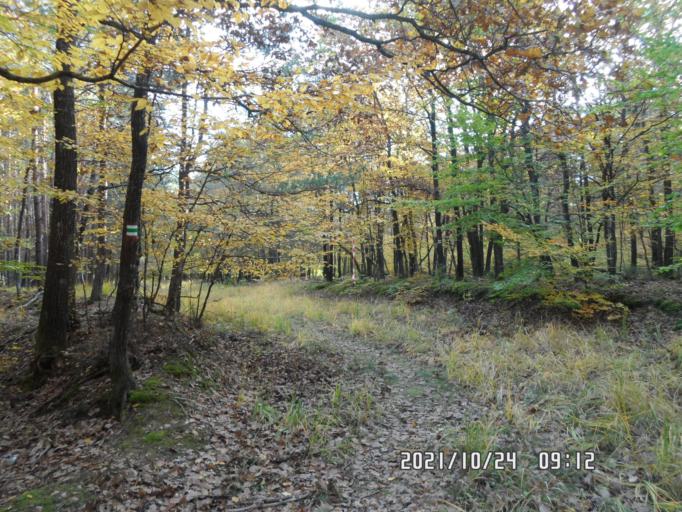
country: SI
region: Hodos-Hodos
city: Hodos
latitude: 46.8430
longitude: 16.3412
